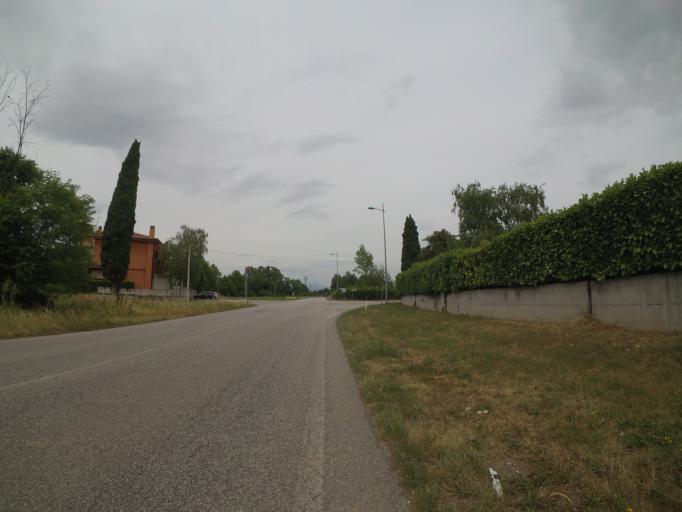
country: IT
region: Friuli Venezia Giulia
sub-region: Provincia di Udine
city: Basiliano-Vissandone
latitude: 46.0363
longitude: 13.1008
